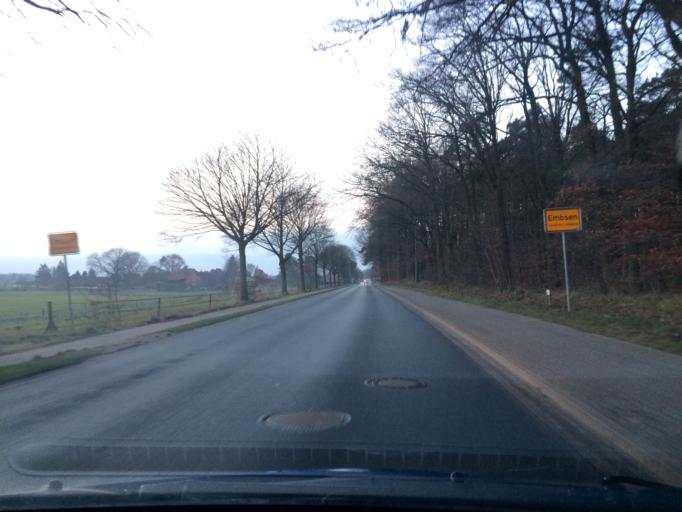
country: DE
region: Lower Saxony
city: Embsen
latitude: 53.1810
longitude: 10.3672
